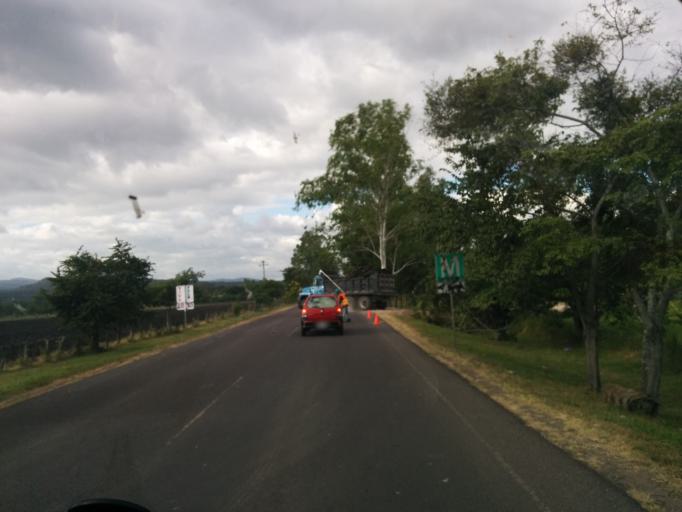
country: NI
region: Esteli
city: Esteli
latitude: 13.1466
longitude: -86.3684
